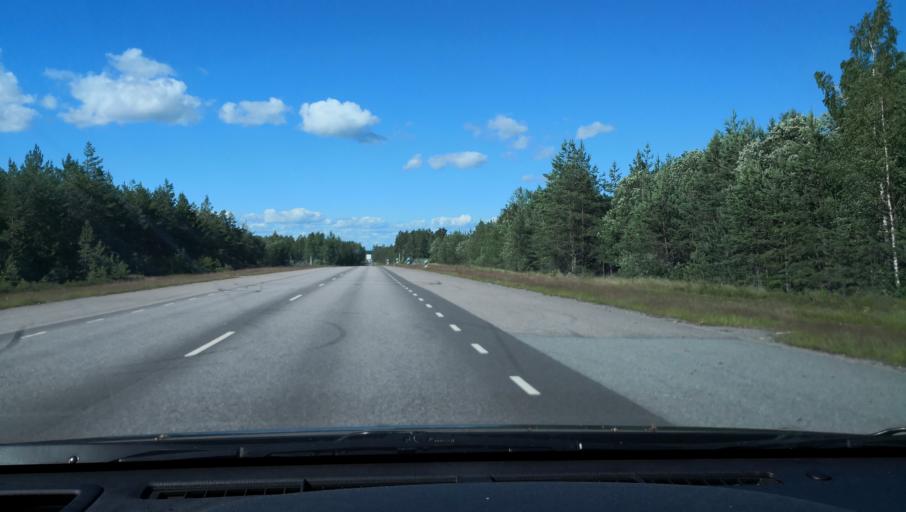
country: SE
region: Soedermanland
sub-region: Eskilstuna Kommun
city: Arla
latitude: 59.3317
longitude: 16.6861
